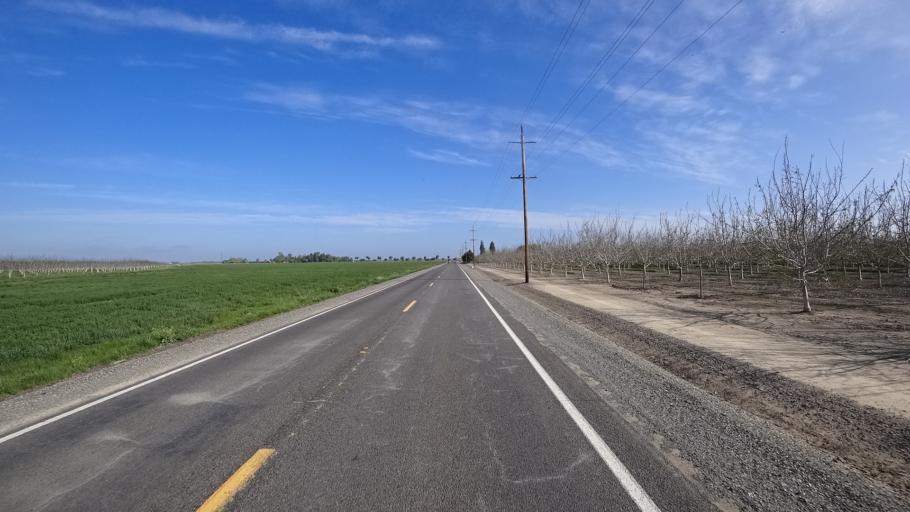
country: US
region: California
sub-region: Glenn County
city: Hamilton City
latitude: 39.5981
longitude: -122.0077
